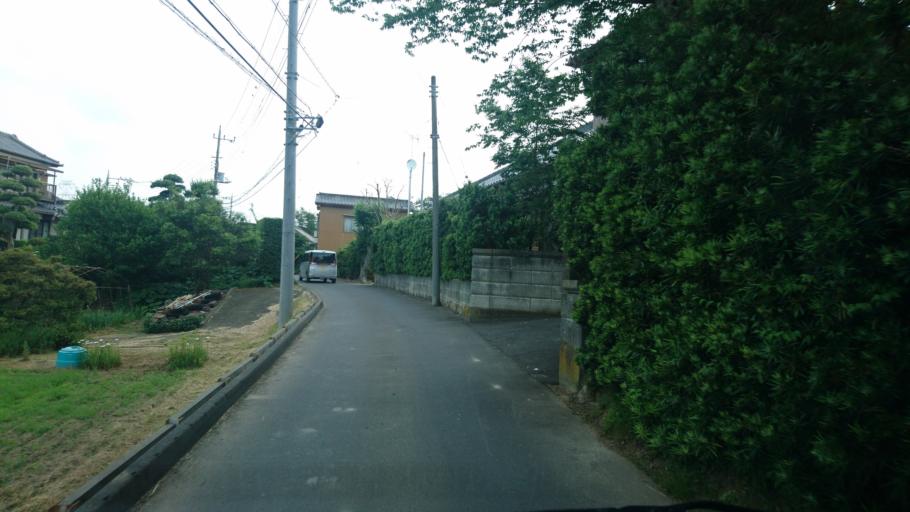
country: JP
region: Ibaraki
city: Edosaki
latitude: 35.8815
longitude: 140.3361
